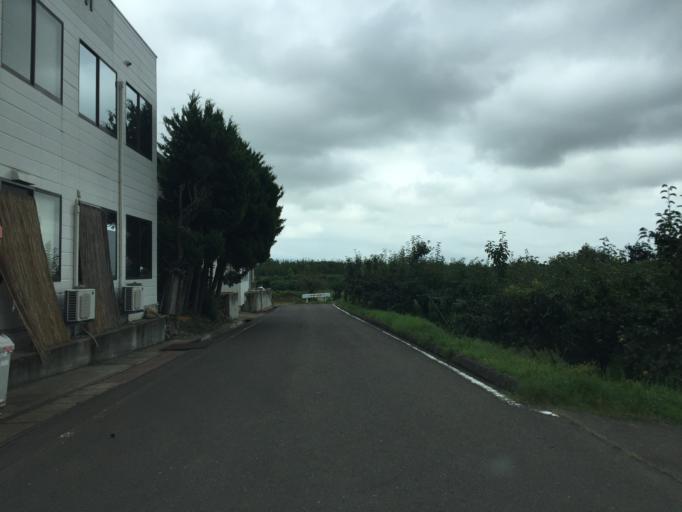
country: JP
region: Fukushima
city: Fukushima-shi
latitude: 37.7857
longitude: 140.3832
